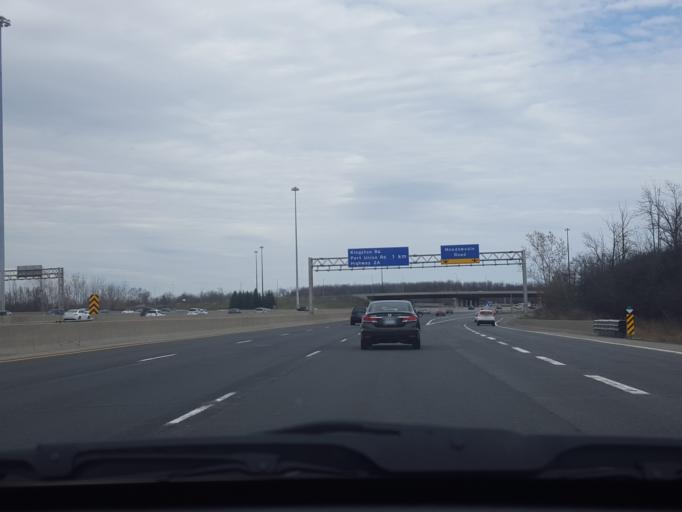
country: CA
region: Ontario
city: Scarborough
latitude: 43.7995
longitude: -79.1731
